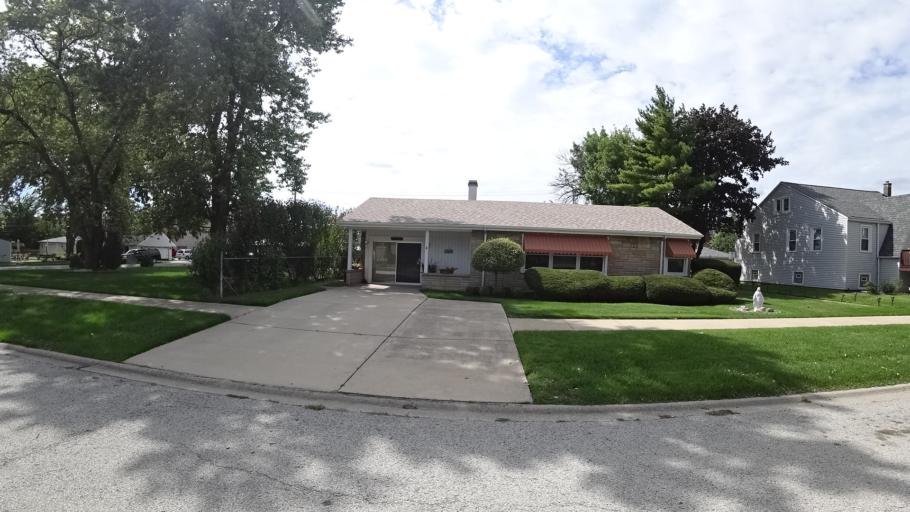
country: US
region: Illinois
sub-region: Cook County
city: Chicago Ridge
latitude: 41.7144
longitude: -87.7785
